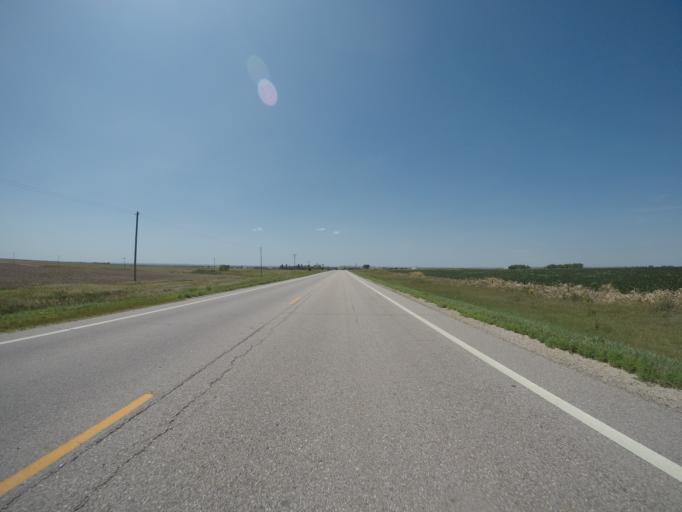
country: US
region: Kansas
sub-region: Osborne County
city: Osborne
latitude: 39.4615
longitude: -98.6946
